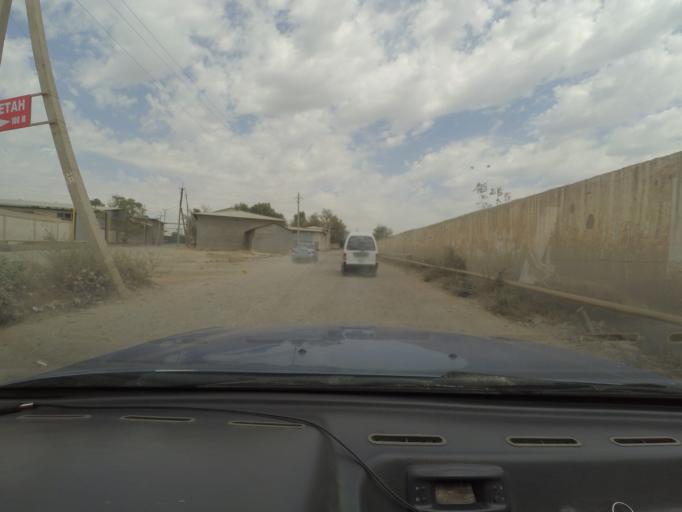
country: UZ
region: Toshkent
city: Urtaowul
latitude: 41.2322
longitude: 69.1533
